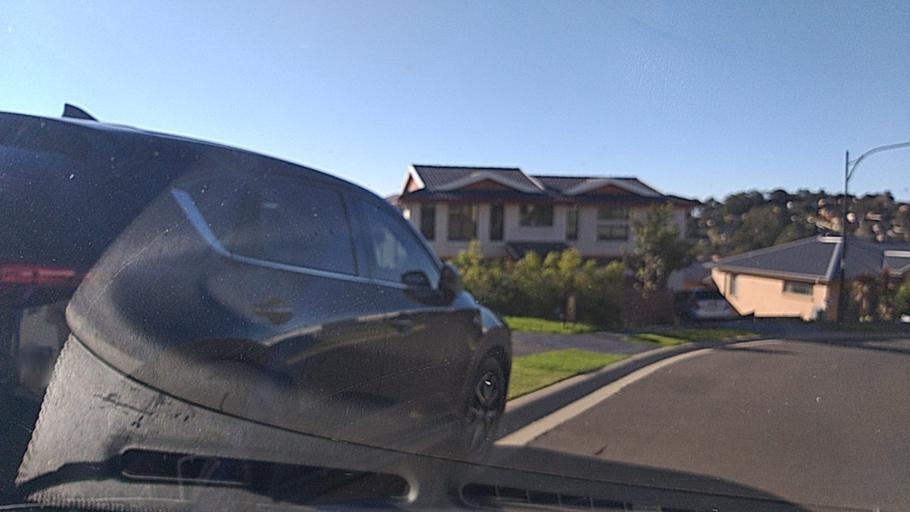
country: AU
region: New South Wales
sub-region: Wollongong
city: Cordeaux Heights
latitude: -34.4395
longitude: 150.8430
